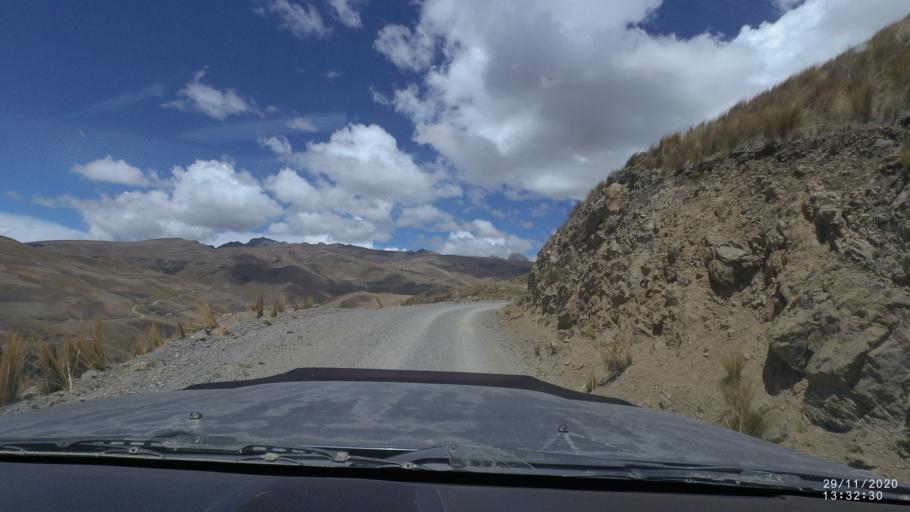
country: BO
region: Cochabamba
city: Cochabamba
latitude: -17.1065
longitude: -66.3416
